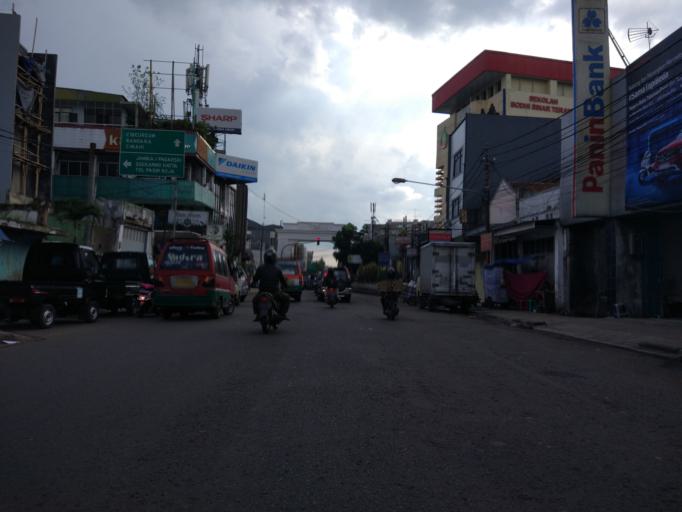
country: ID
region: West Java
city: Bandung
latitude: -6.9188
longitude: 107.5877
